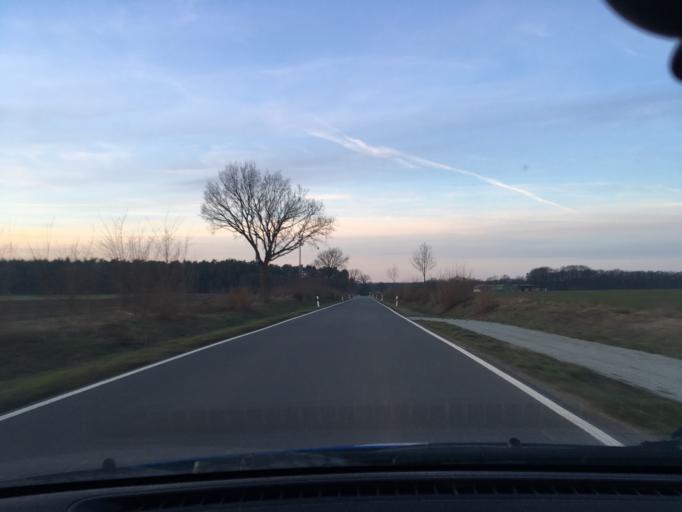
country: DE
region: Schleswig-Holstein
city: Besenthal
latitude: 53.5373
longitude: 10.7403
